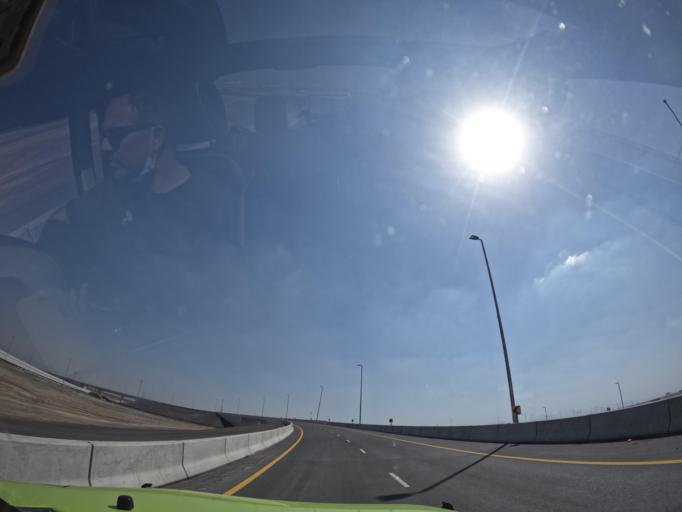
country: AE
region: Ash Shariqah
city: Adh Dhayd
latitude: 24.9083
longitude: 55.7991
